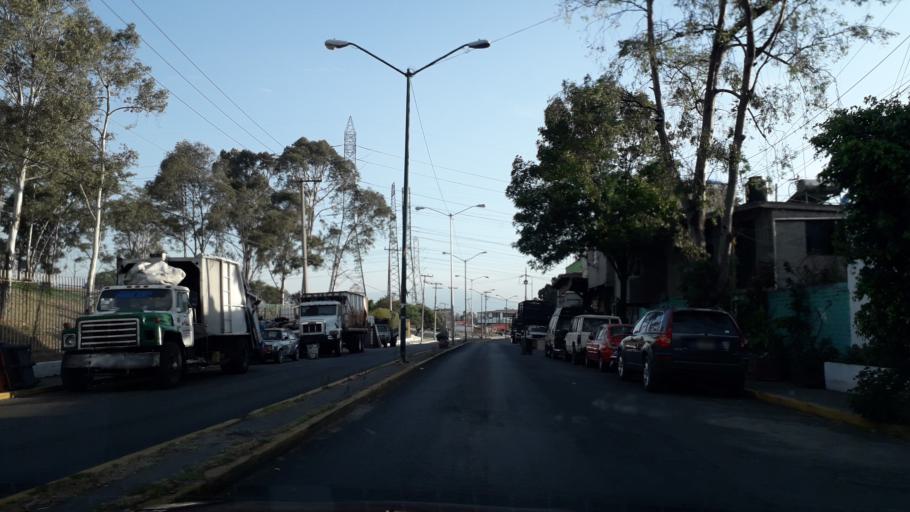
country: MX
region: Mexico City
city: Iztapalapa
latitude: 19.3649
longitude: -99.0480
